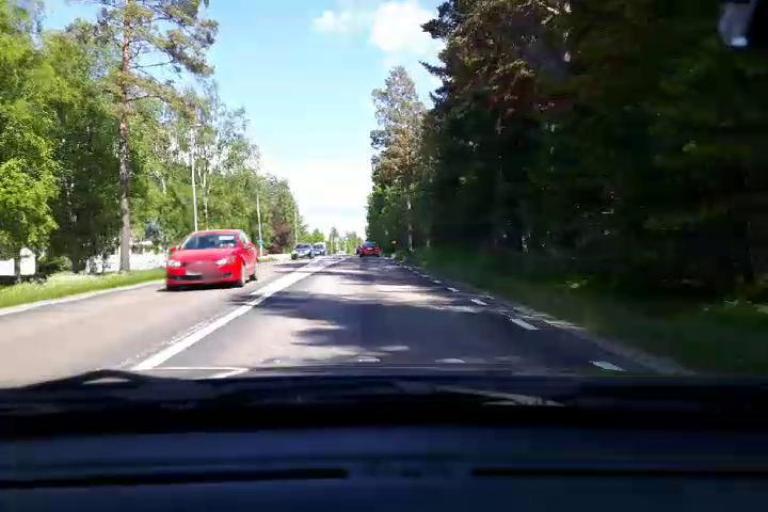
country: SE
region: Gaevleborg
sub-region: Hudiksvalls Kommun
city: Delsbo
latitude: 61.7985
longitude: 16.5412
